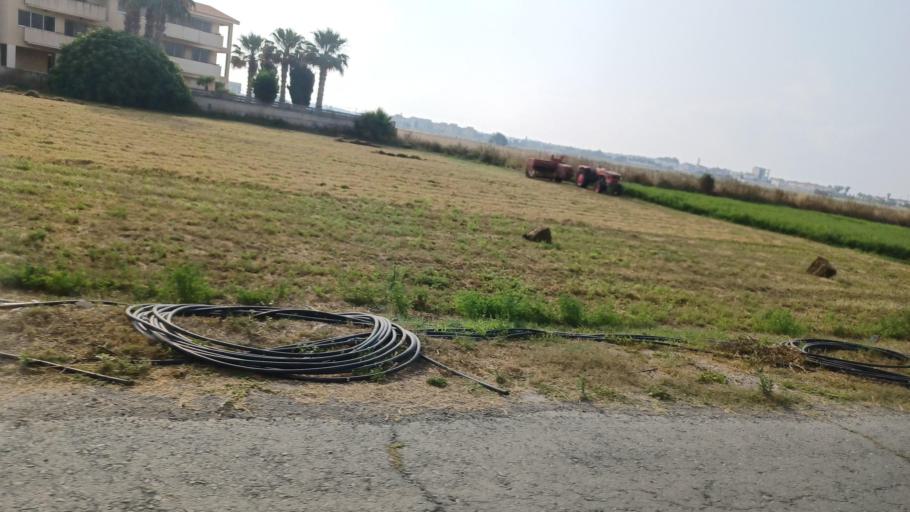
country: CY
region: Larnaka
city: Perivolia
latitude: 34.8257
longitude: 33.5780
